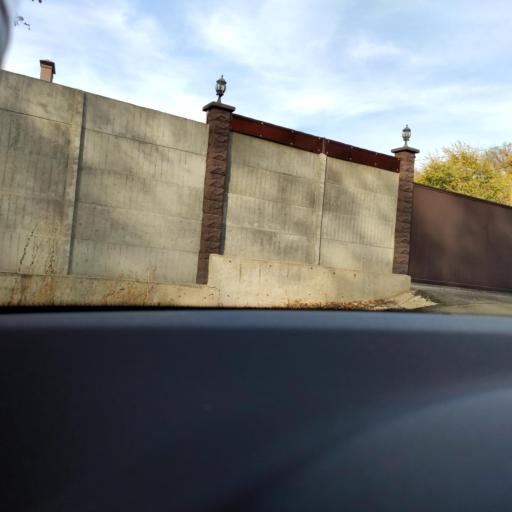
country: RU
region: Samara
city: Samara
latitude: 53.2650
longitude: 50.1842
